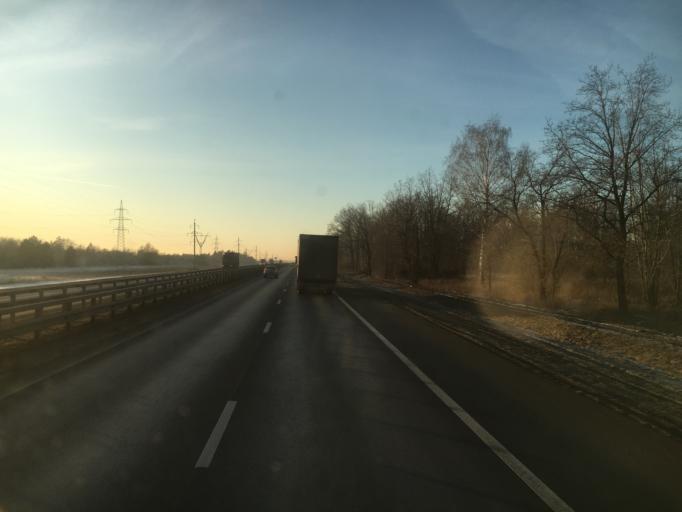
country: RU
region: Samara
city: Pribrezhnyy
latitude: 53.5186
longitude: 49.8055
